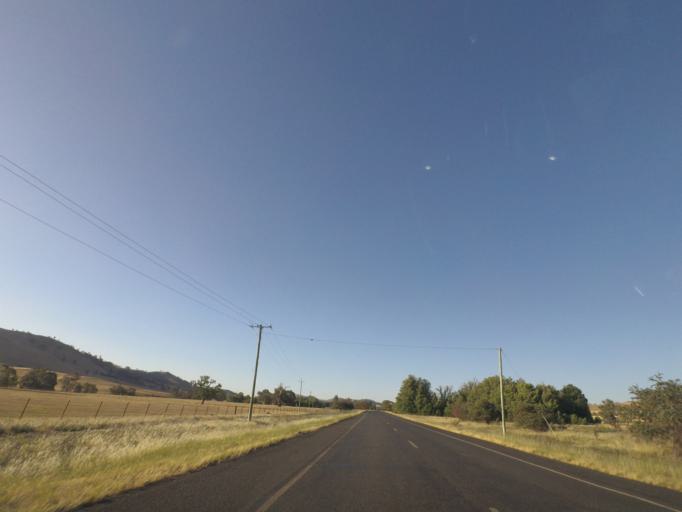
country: AU
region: New South Wales
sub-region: Gundagai
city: Gundagai
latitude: -34.9391
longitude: 148.1678
